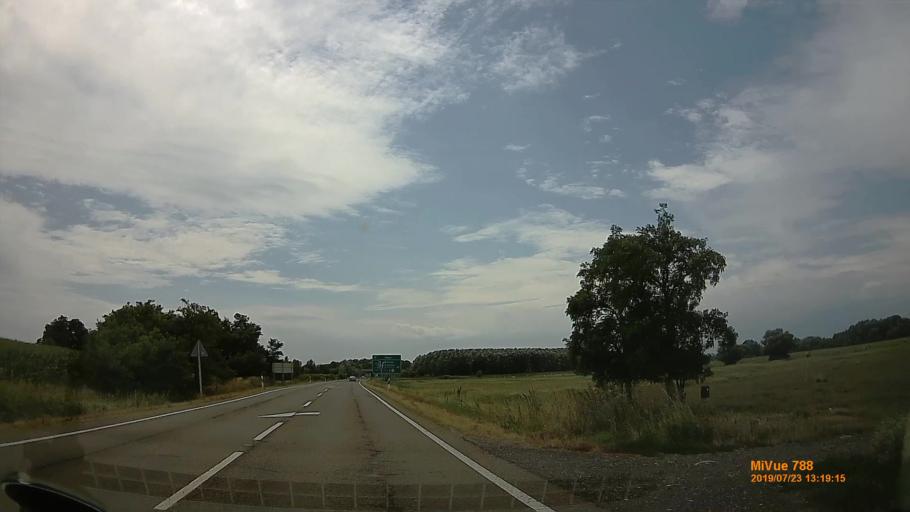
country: HU
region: Hajdu-Bihar
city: Polgar
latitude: 47.8756
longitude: 21.1424
